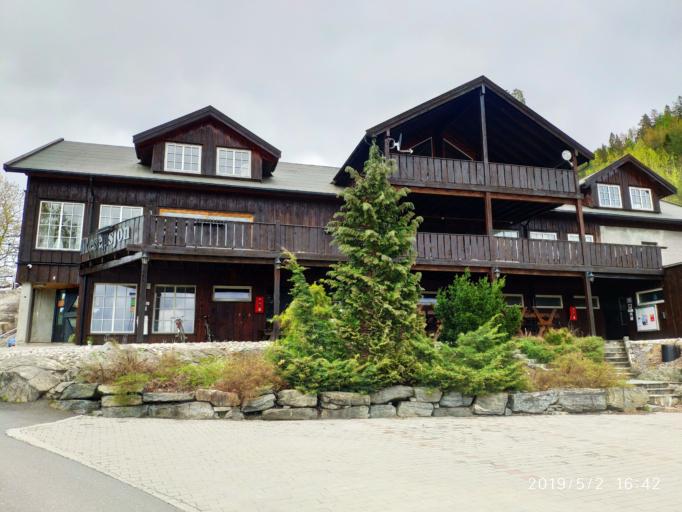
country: NO
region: Telemark
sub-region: Kragero
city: Kragero
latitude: 58.9016
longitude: 9.4088
